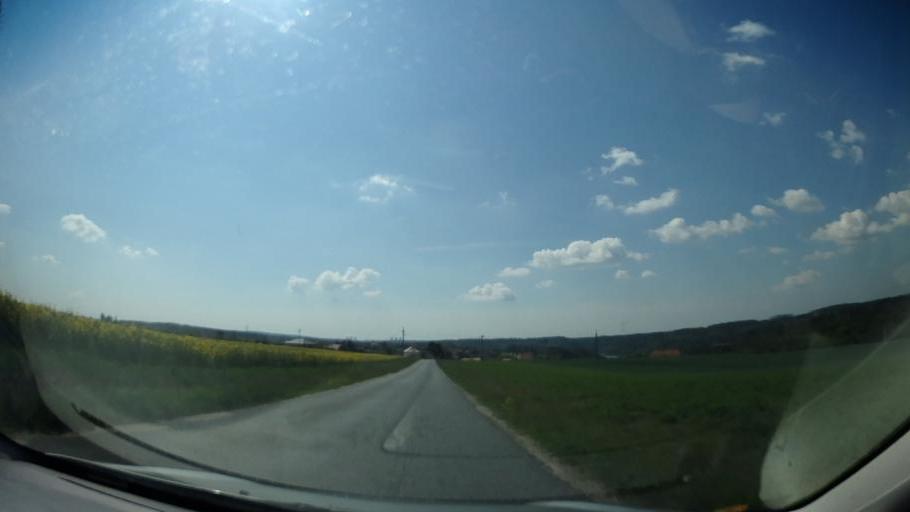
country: CZ
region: Vysocina
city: Hrotovice
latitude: 49.1767
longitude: 16.0839
